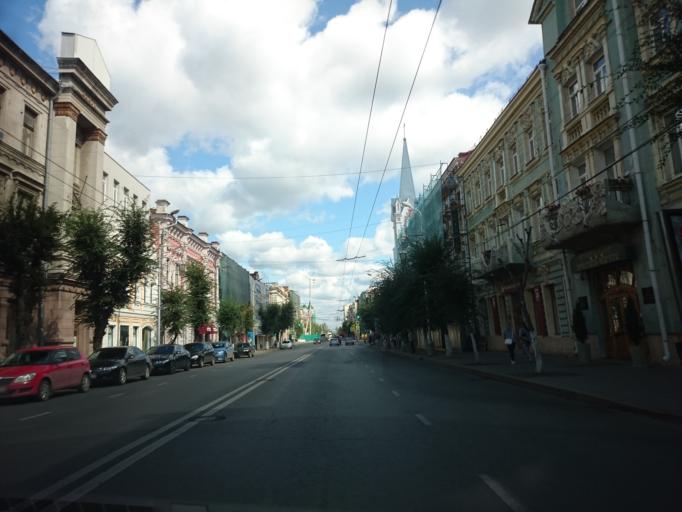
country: RU
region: Samara
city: Rozhdestveno
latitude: 53.1893
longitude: 50.0901
